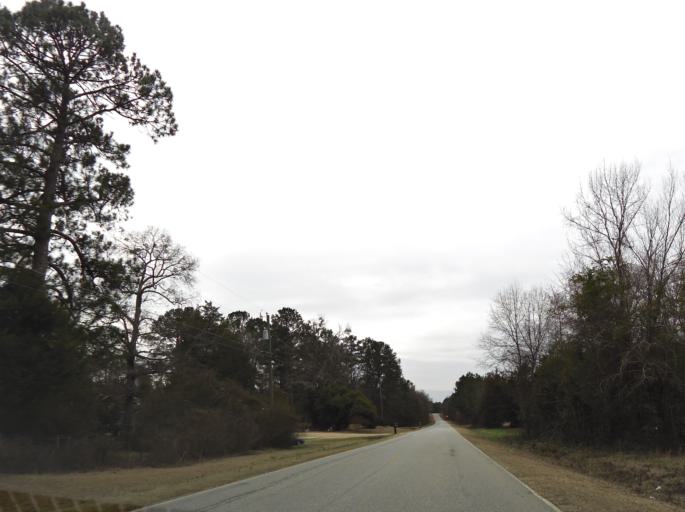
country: US
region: Georgia
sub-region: Peach County
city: Byron
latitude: 32.6117
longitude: -83.7882
